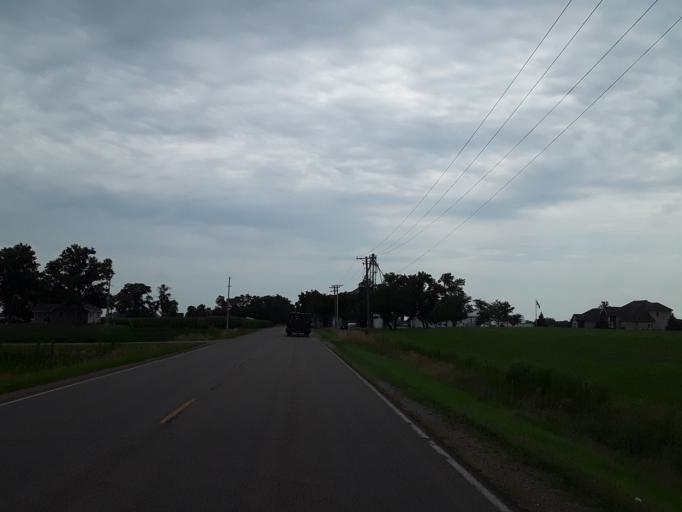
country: US
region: Nebraska
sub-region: Douglas County
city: Valley
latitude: 41.2559
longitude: -96.3305
